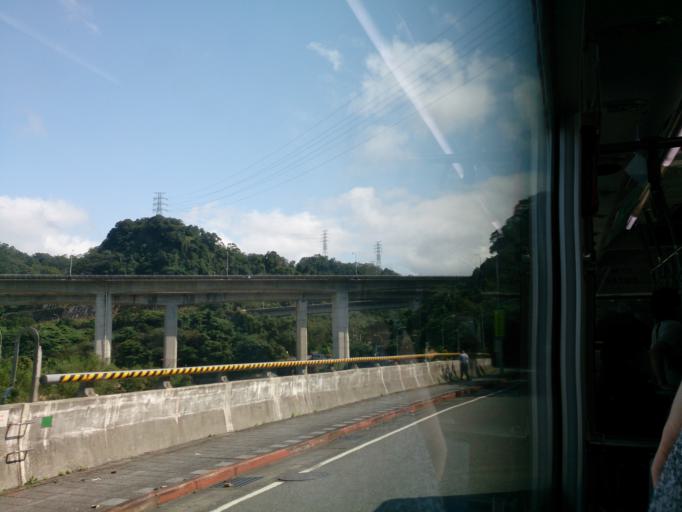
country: TW
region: Taipei
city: Taipei
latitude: 24.9975
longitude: 121.5915
